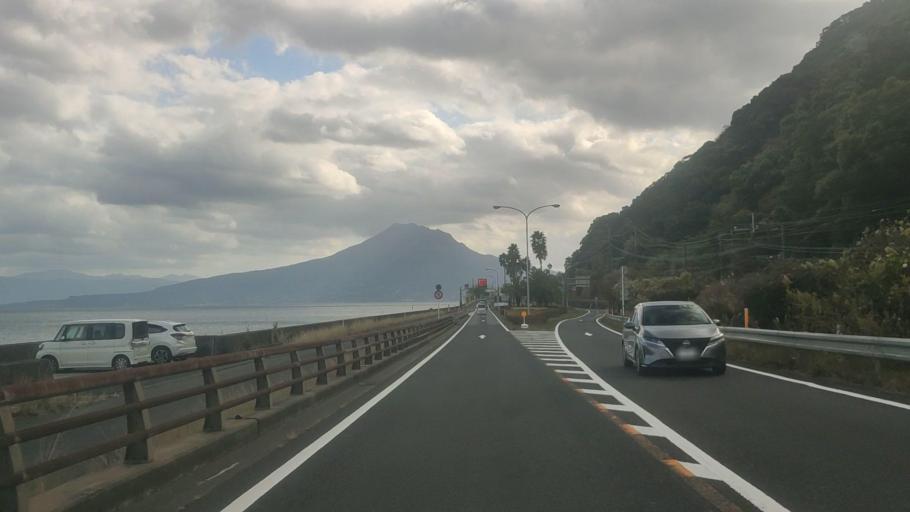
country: JP
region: Kagoshima
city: Kajiki
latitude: 31.6964
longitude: 130.6140
